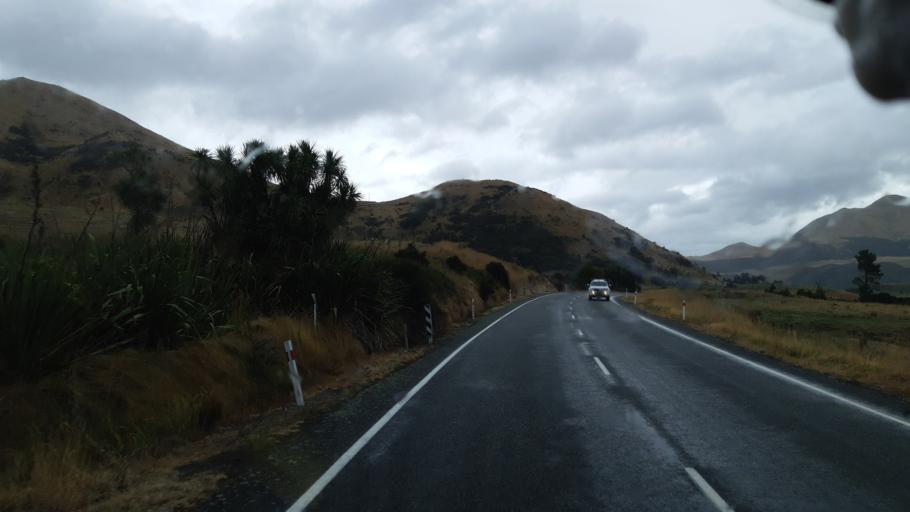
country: NZ
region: Canterbury
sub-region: Hurunui District
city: Amberley
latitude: -42.6406
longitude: 172.7705
